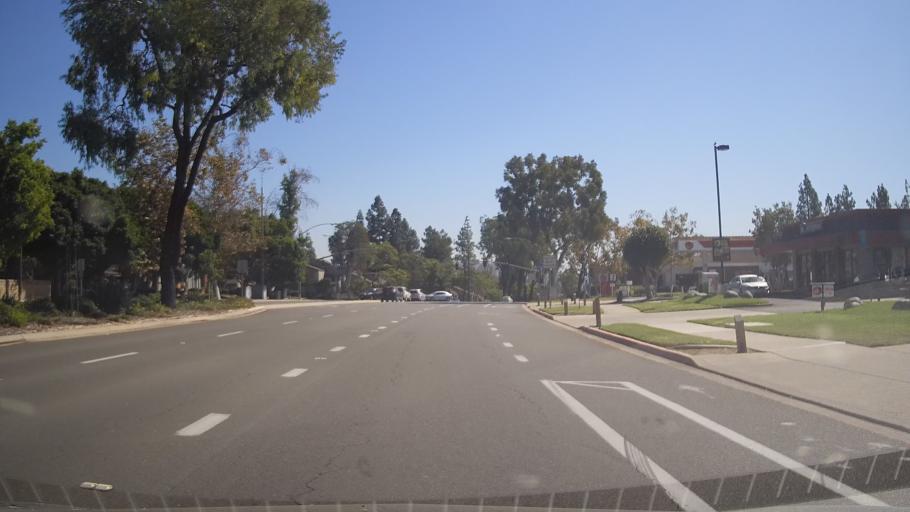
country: US
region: California
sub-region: San Diego County
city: La Mesa
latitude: 32.8219
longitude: -117.0990
